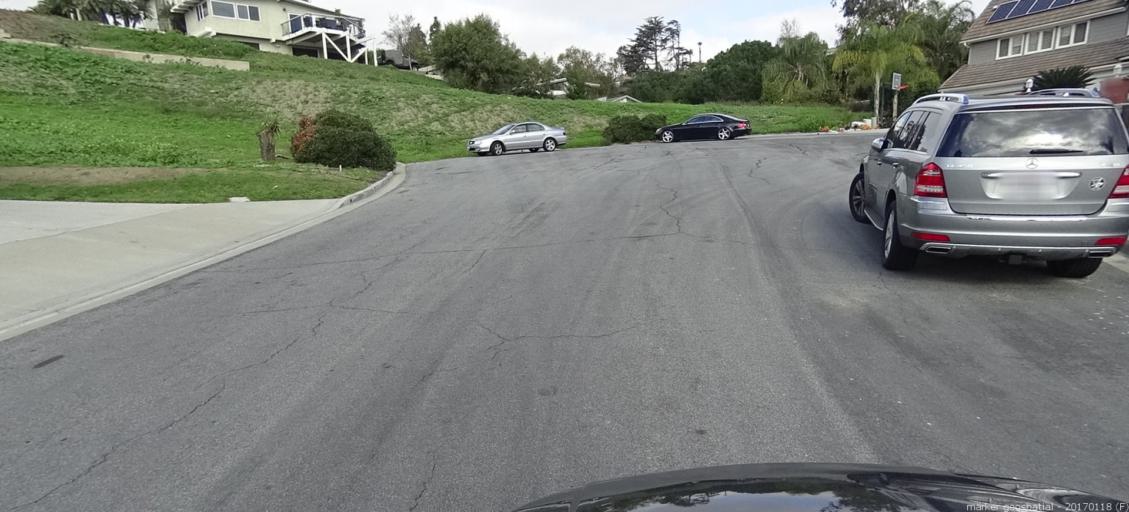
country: US
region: California
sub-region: Orange County
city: North Tustin
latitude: 33.7713
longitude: -117.7937
